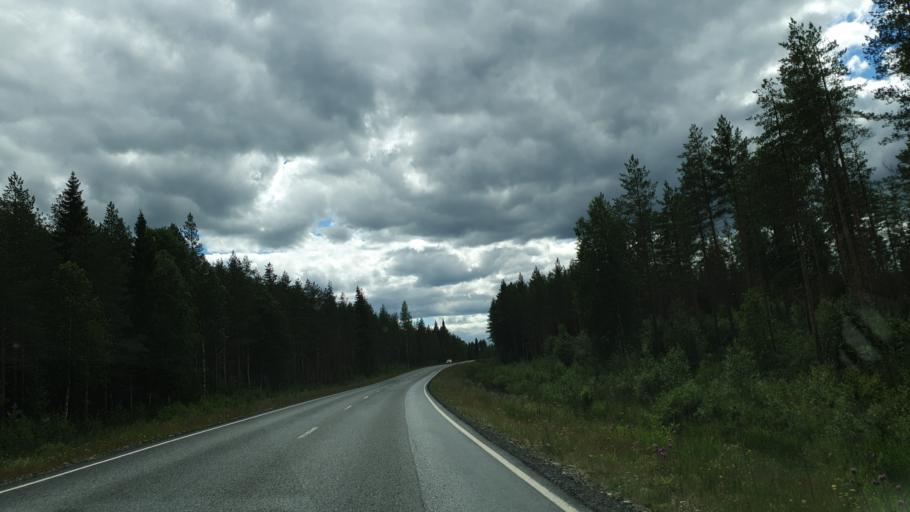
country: FI
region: Kainuu
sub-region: Kehys-Kainuu
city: Kuhmo
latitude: 64.0256
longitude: 29.5950
